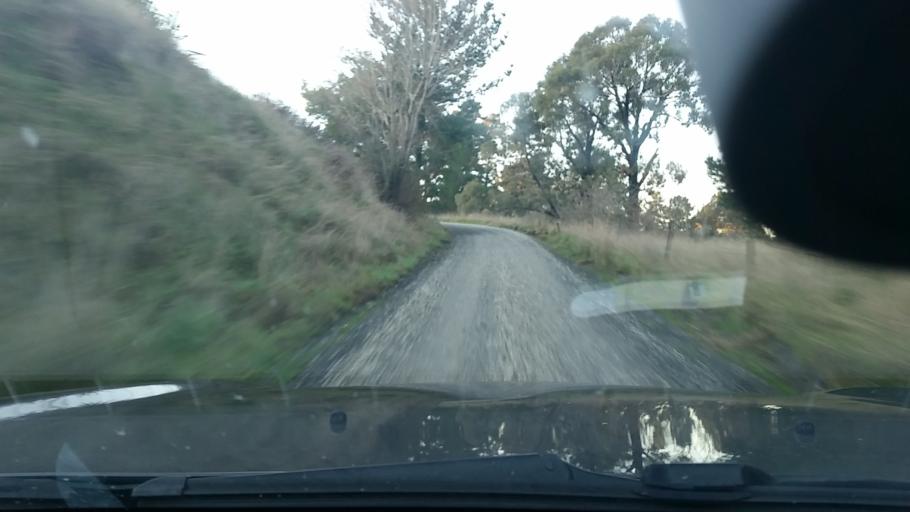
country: NZ
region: Marlborough
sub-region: Marlborough District
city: Blenheim
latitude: -41.7298
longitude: 174.0368
